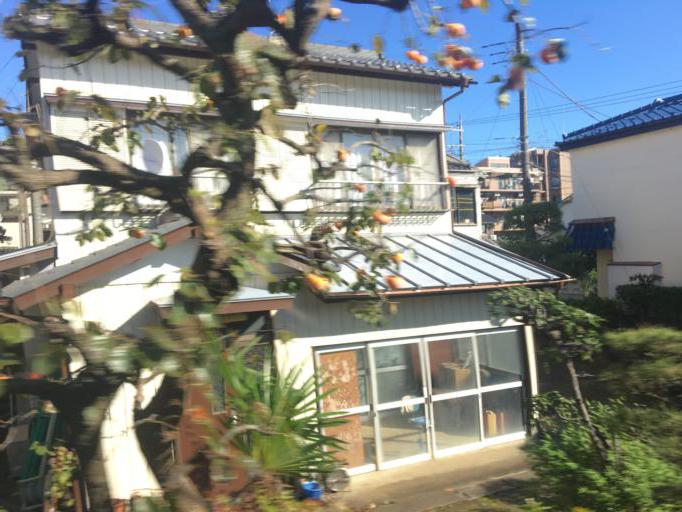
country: JP
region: Chiba
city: Funabashi
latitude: 35.7128
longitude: 139.9573
